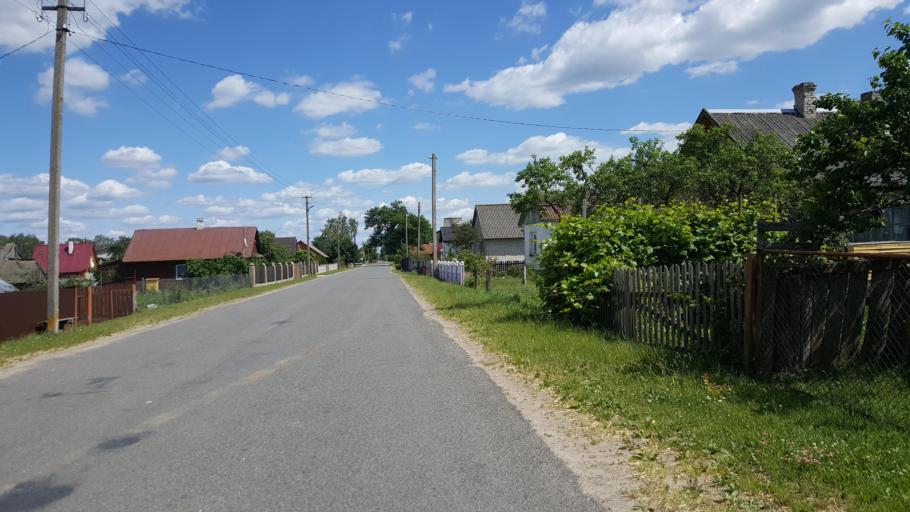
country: PL
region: Podlasie
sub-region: Powiat hajnowski
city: Czeremcha
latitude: 52.5381
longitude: 23.5452
